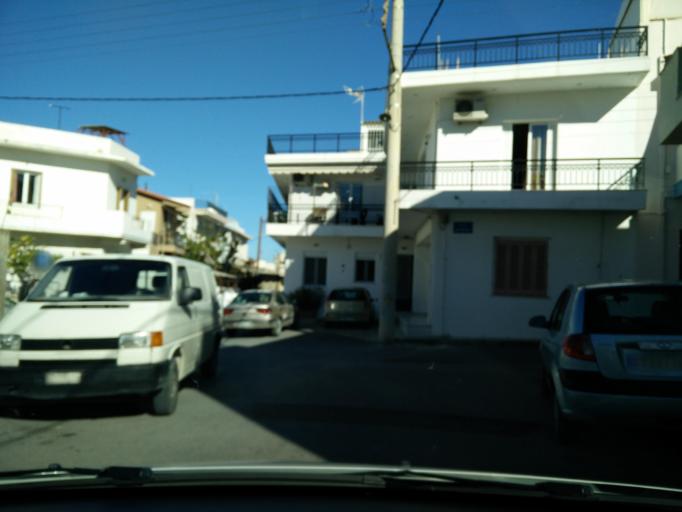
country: GR
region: Crete
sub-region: Nomos Irakleiou
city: Nea Alikarnassos
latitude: 35.3385
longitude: 25.1498
